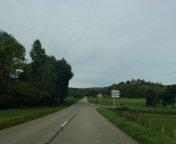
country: FR
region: Bourgogne
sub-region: Departement de Saone-et-Loire
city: Cuiseaux
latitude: 46.4630
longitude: 5.4469
